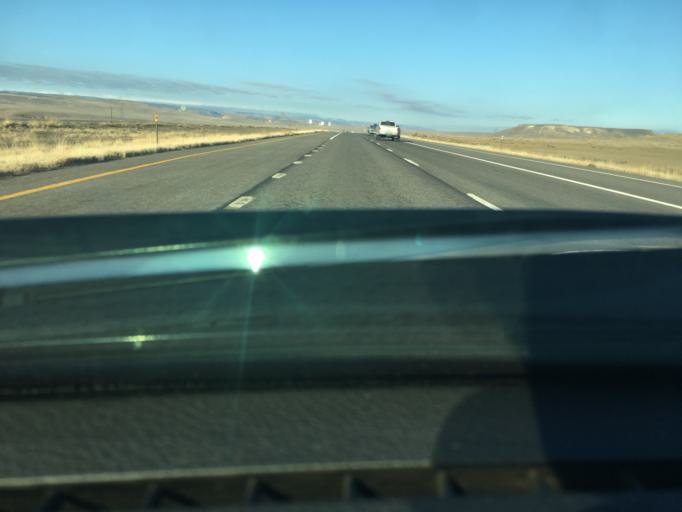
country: US
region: Colorado
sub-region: Delta County
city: Delta
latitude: 38.7561
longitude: -108.1769
